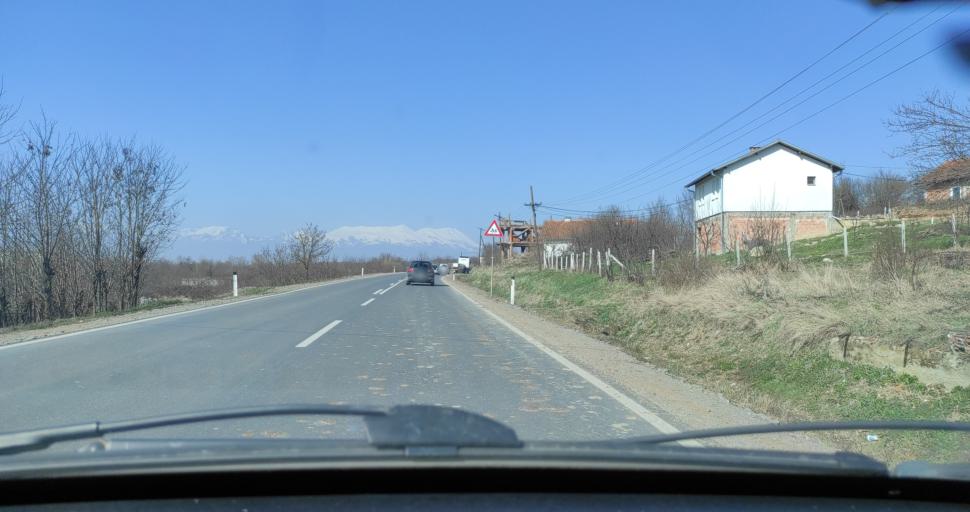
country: XK
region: Pec
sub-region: Komuna e Klines
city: Klina
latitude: 42.6021
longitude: 20.5228
